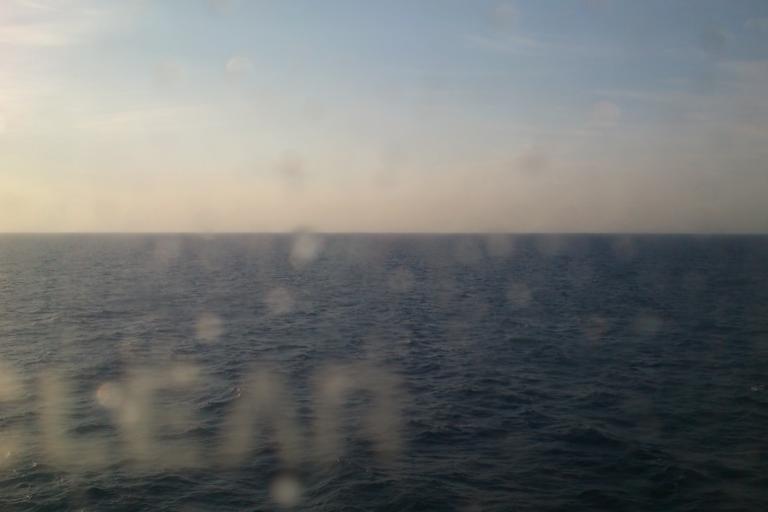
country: JP
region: Ishikawa
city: Nanao
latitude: 37.7336
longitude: 136.3971
